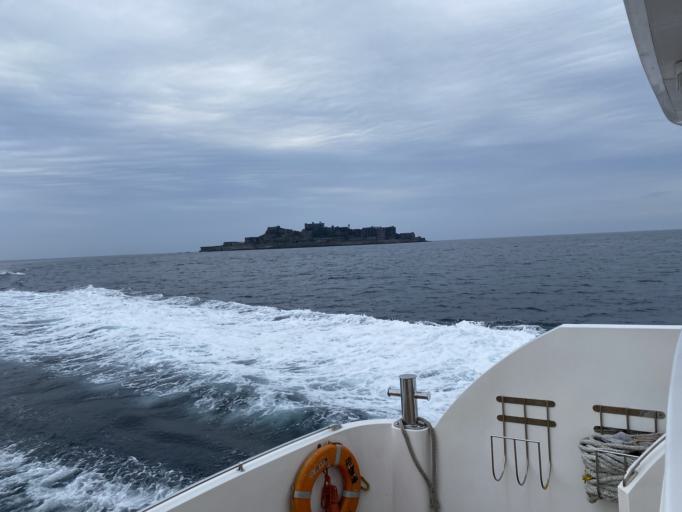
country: JP
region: Nagasaki
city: Nagasaki-shi
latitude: 32.6245
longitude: 129.7493
